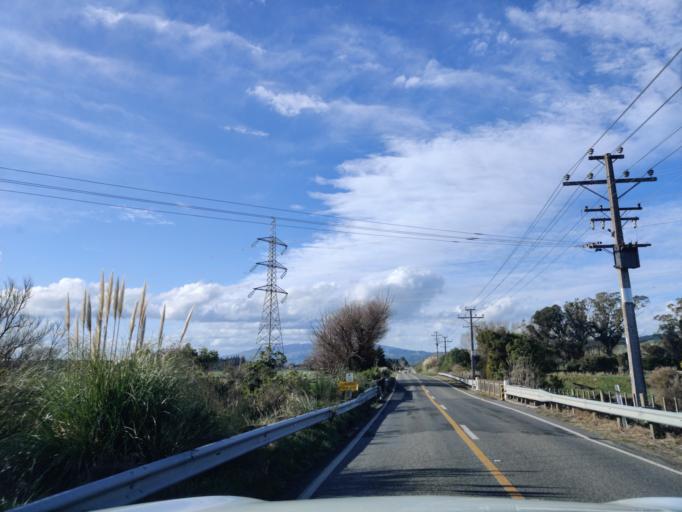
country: NZ
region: Manawatu-Wanganui
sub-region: Palmerston North City
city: Palmerston North
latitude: -40.3444
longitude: 175.7105
